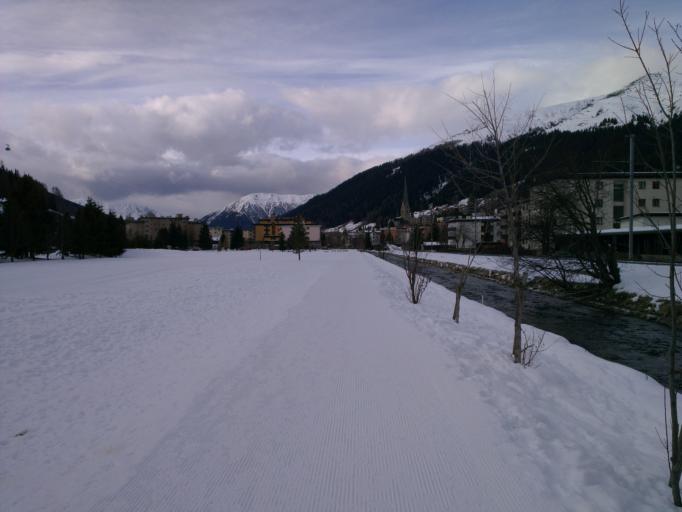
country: CH
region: Grisons
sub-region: Praettigau/Davos District
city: Davos
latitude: 46.7972
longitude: 9.8303
